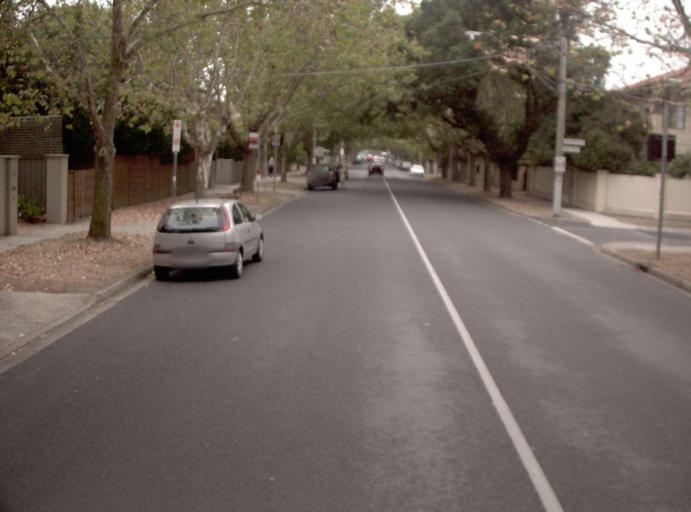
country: AU
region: Victoria
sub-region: Port Phillip
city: St Kilda East
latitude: -37.8574
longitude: 145.0110
